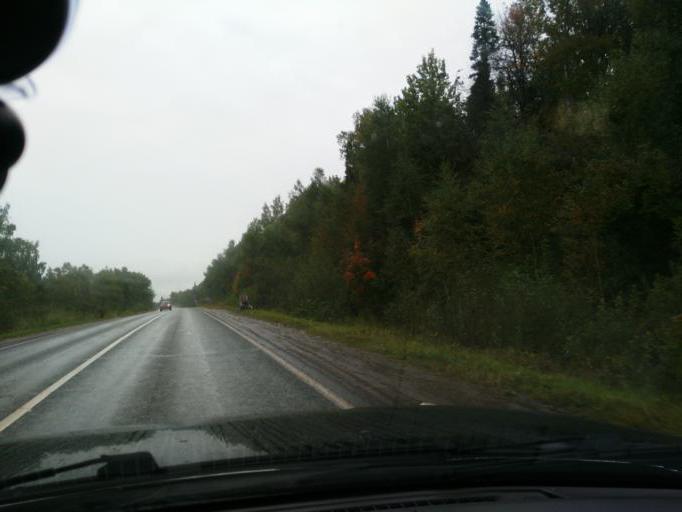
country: RU
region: Perm
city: Yugo-Kamskiy
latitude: 57.5803
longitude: 55.6784
